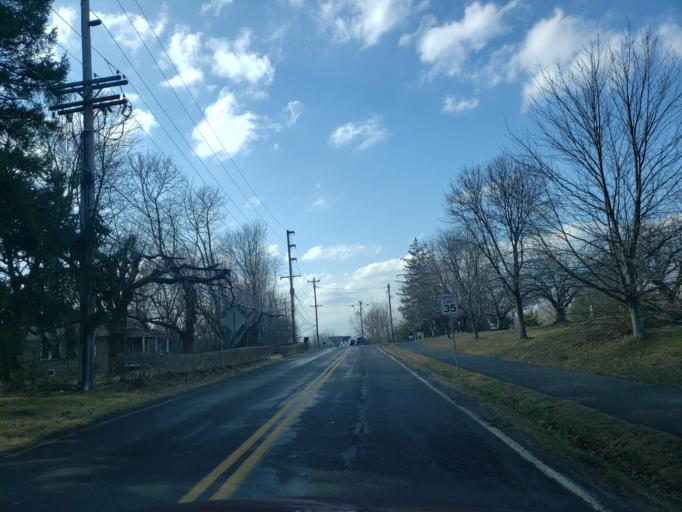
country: US
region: Pennsylvania
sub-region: Bucks County
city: Doylestown
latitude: 40.2913
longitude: -75.1298
